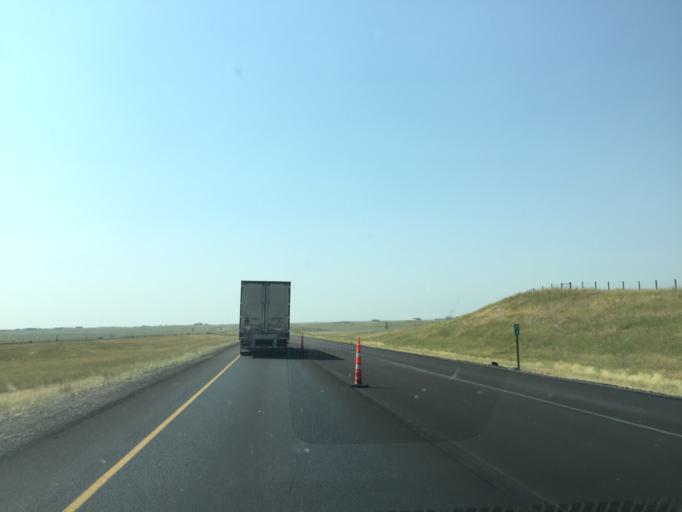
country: US
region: Wyoming
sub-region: Laramie County
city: Ranchettes
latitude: 41.3149
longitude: -104.8591
